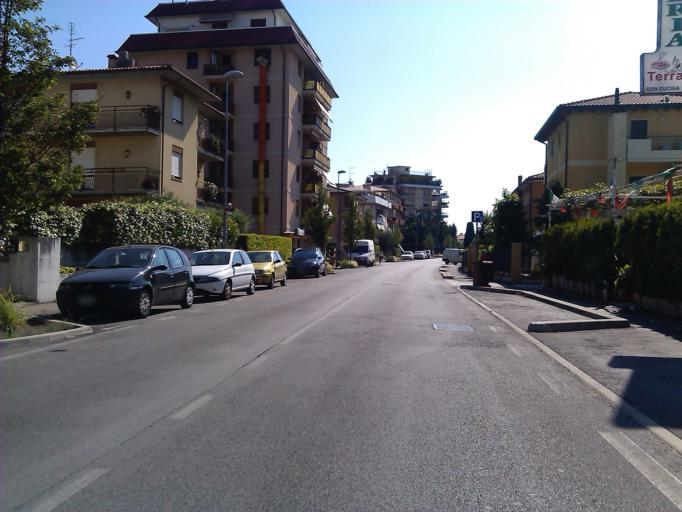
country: IT
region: Veneto
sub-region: Provincia di Vicenza
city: Bassano del Grappa
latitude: 45.7718
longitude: 11.7461
